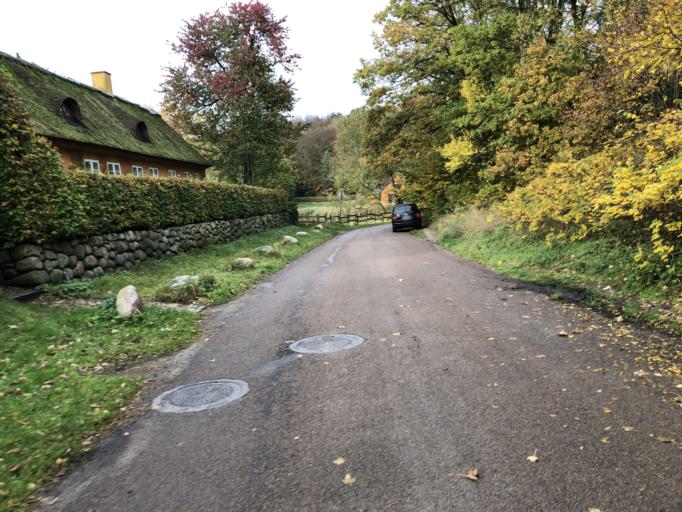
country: DK
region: Capital Region
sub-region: Lyngby-Tarbaek Kommune
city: Kongens Lyngby
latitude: 55.8007
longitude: 12.5140
